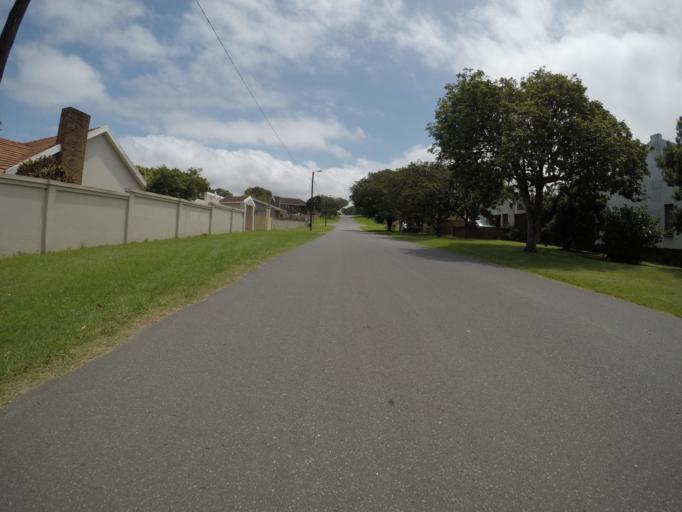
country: ZA
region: Eastern Cape
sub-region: Buffalo City Metropolitan Municipality
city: East London
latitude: -32.9426
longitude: 28.0078
